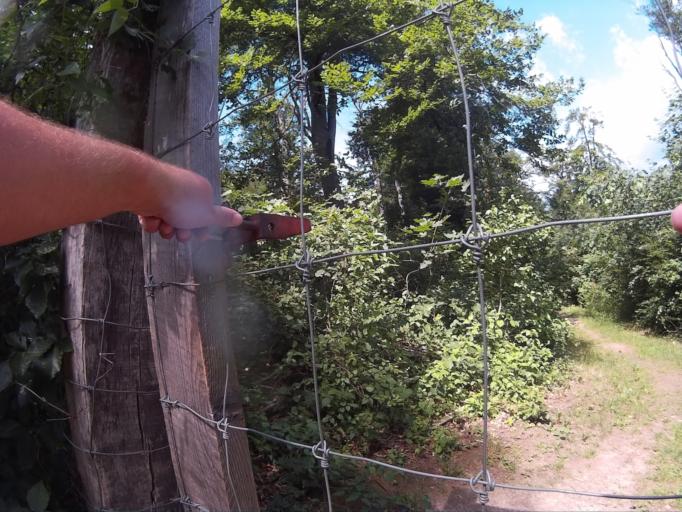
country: HU
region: Veszprem
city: Herend
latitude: 47.1084
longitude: 17.7883
